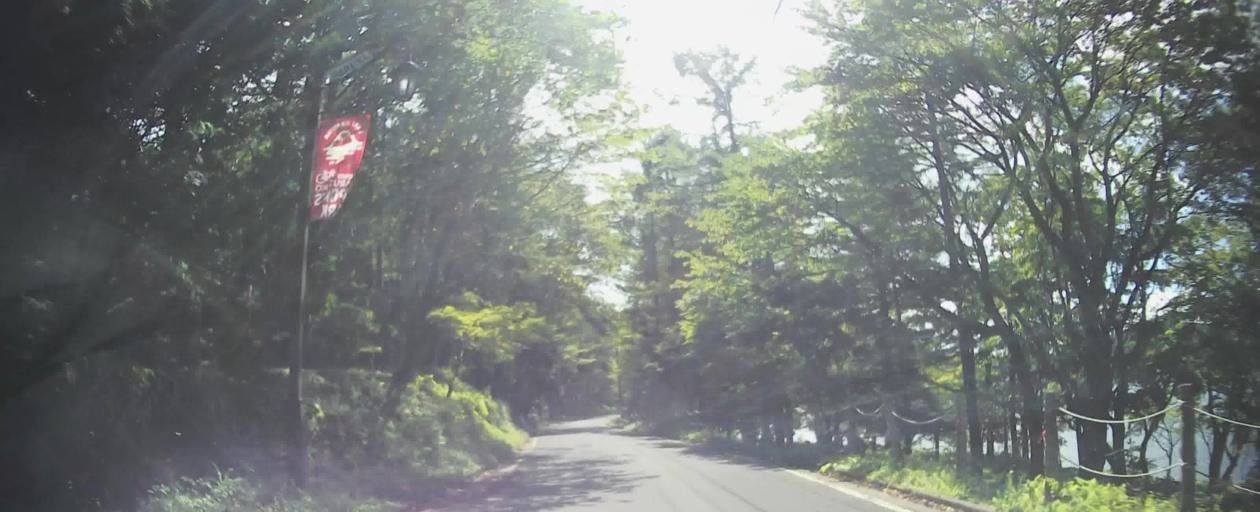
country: JP
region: Gunma
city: Nakanojomachi
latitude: 36.4797
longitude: 138.8723
